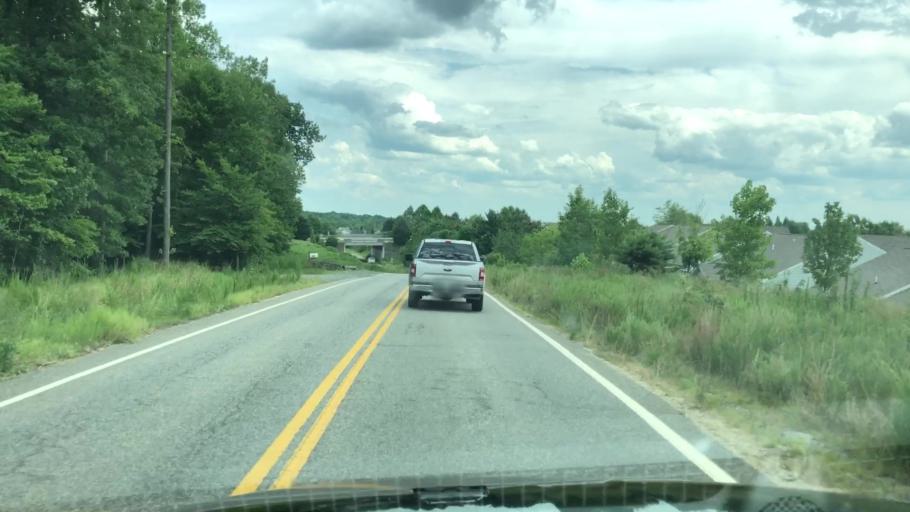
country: US
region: Virginia
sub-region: Stafford County
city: Falmouth
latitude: 38.3388
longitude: -77.5204
